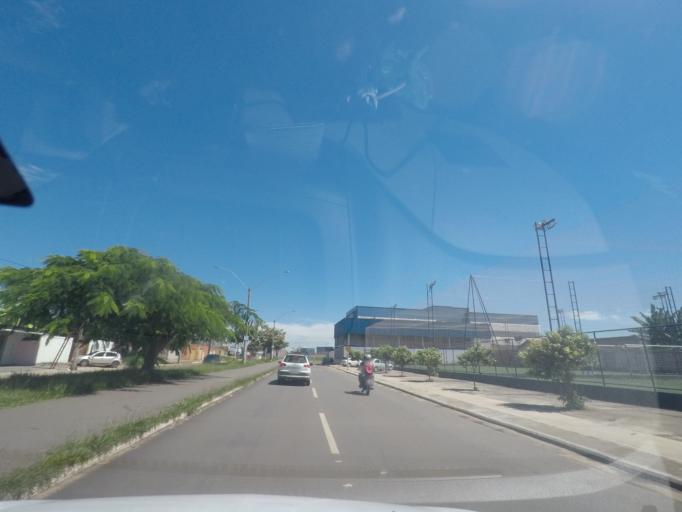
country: BR
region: Goias
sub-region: Aparecida De Goiania
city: Aparecida de Goiania
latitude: -16.7766
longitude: -49.3369
